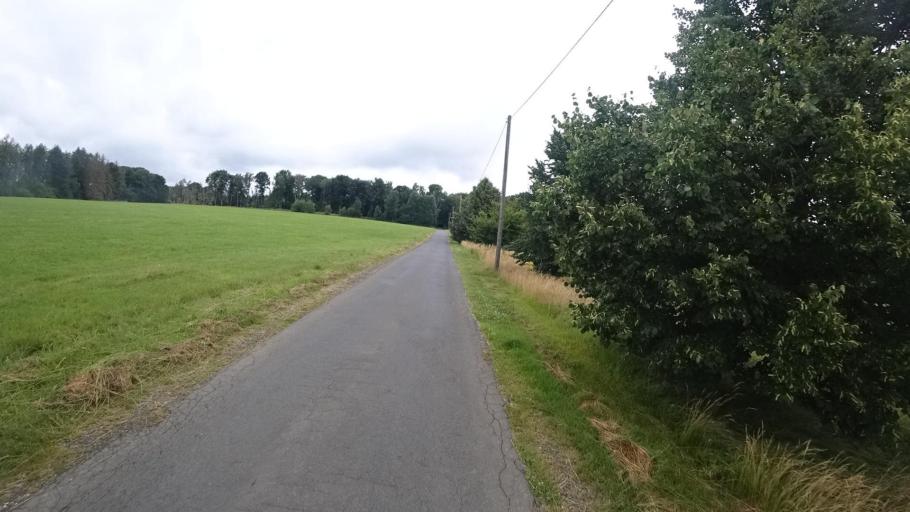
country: DE
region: Rheinland-Pfalz
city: Seifen
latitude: 50.6719
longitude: 7.5130
